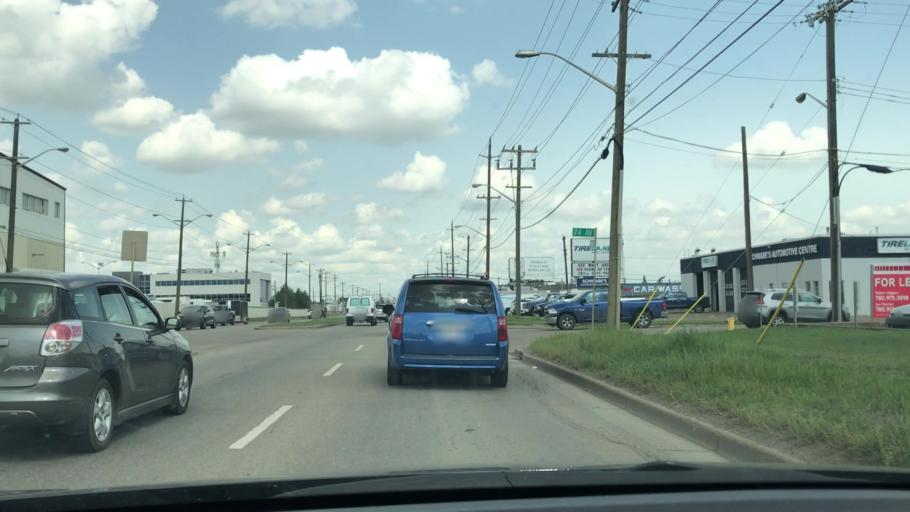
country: CA
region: Alberta
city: Edmonton
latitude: 53.5097
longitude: -113.4183
